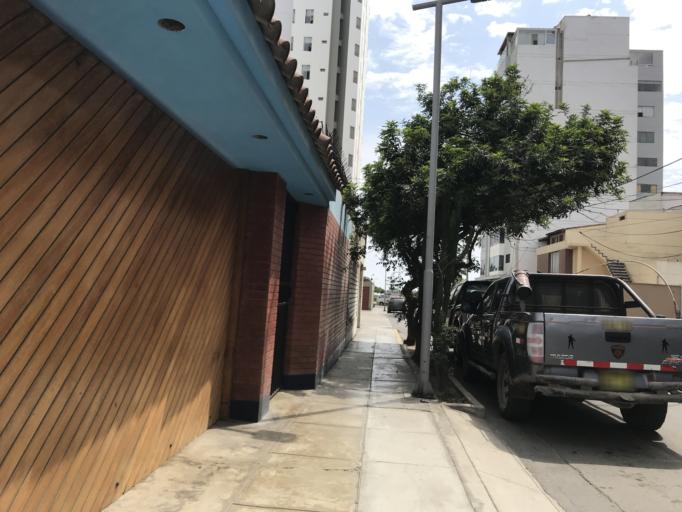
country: PE
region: Lima
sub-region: Lima
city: San Isidro
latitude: -12.1164
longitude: -77.0461
